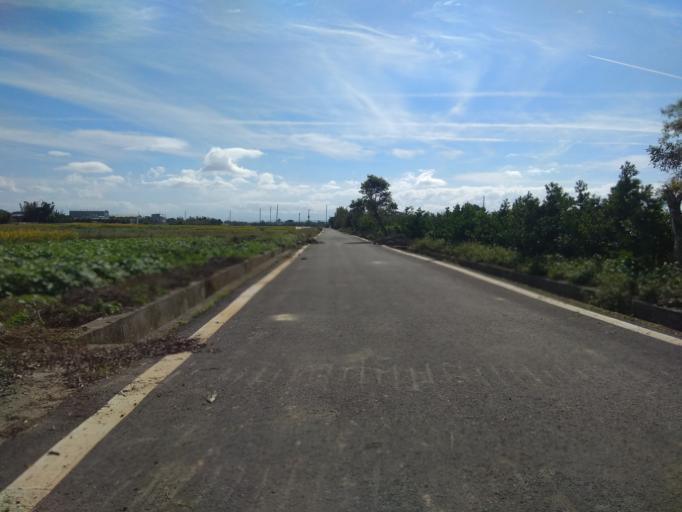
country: TW
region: Taiwan
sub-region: Hsinchu
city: Zhubei
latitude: 24.9977
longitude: 121.0393
